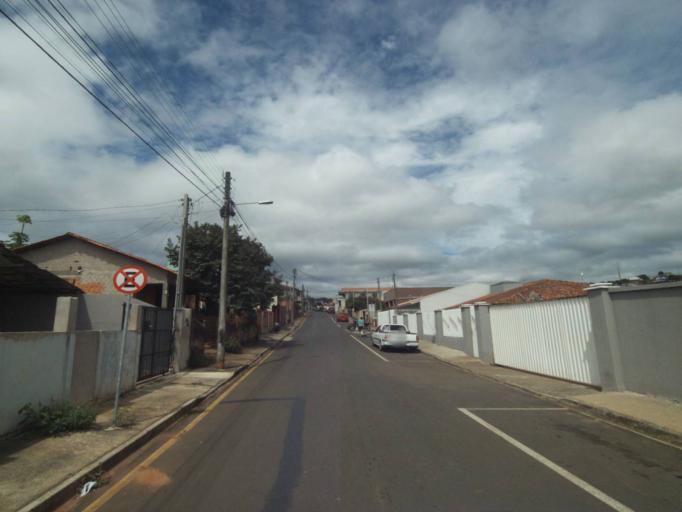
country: BR
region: Parana
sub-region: Telemaco Borba
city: Telemaco Borba
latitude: -24.3296
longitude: -50.6335
